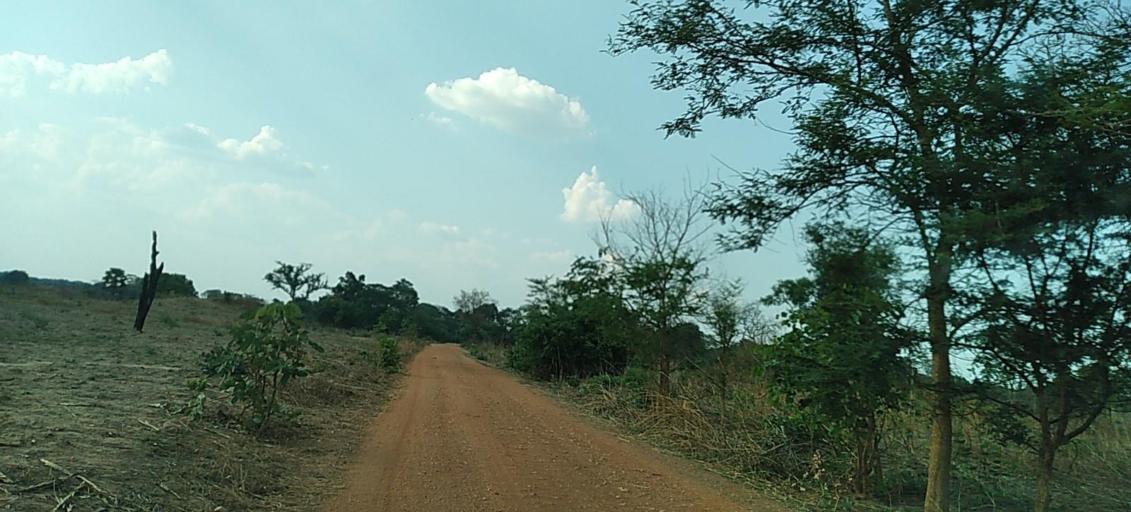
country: ZM
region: Copperbelt
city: Mpongwe
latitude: -13.4911
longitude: 28.0849
